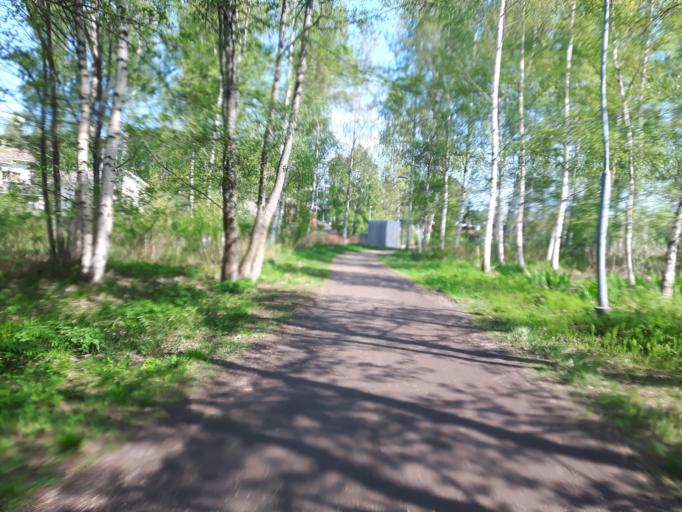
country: FI
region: Uusimaa
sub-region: Helsinki
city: Vantaa
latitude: 60.2153
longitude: 25.1161
